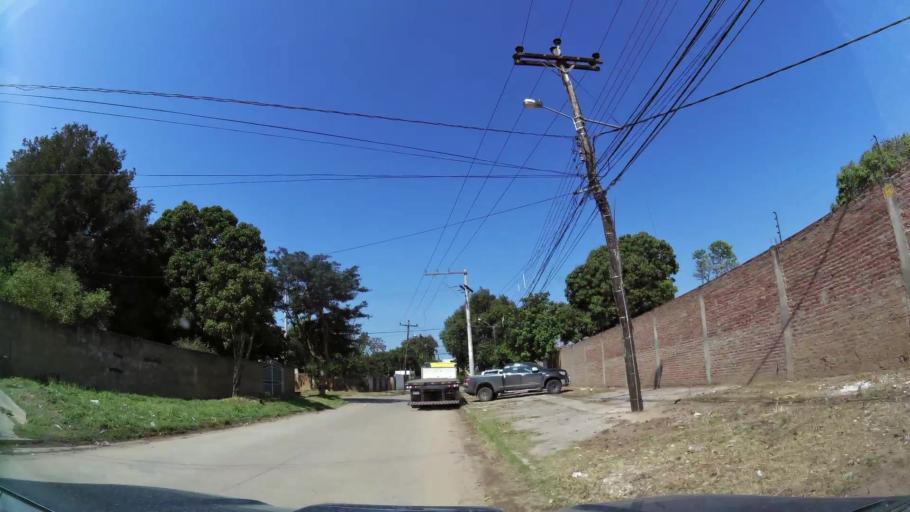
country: BO
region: Santa Cruz
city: Santa Cruz de la Sierra
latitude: -17.7480
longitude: -63.1729
